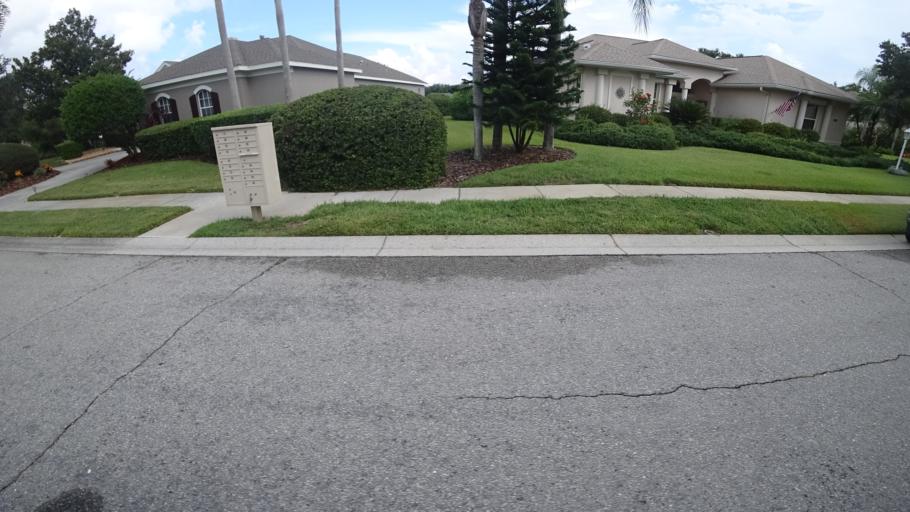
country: US
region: Florida
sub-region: Sarasota County
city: The Meadows
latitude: 27.4160
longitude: -82.4293
